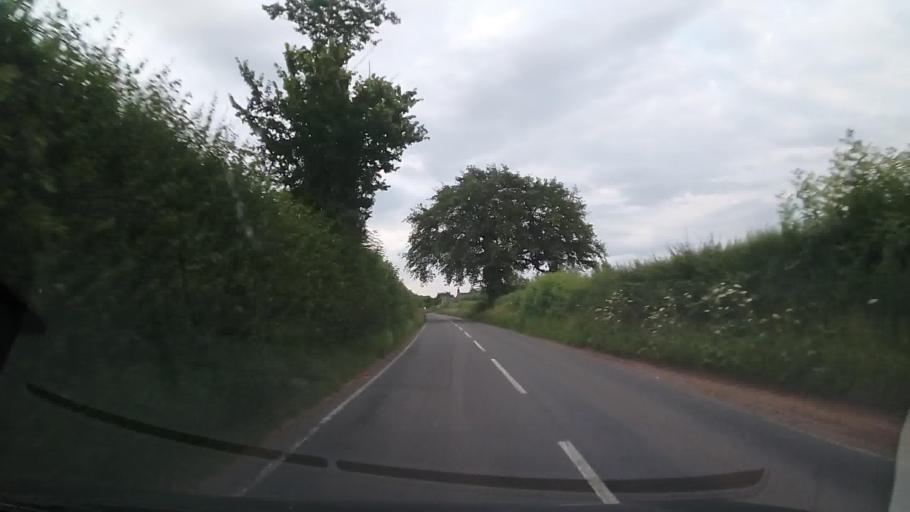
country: GB
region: England
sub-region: Shropshire
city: Great Ness
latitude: 52.7967
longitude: -2.9228
